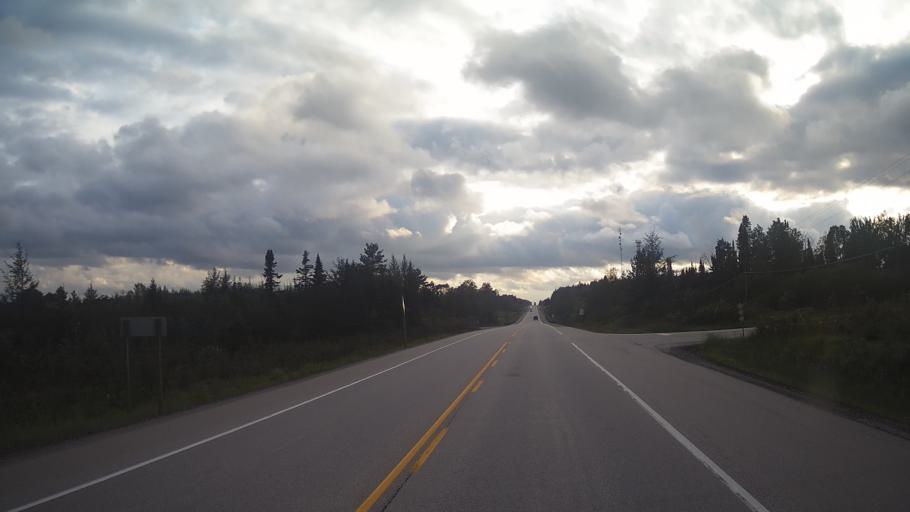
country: CA
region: Ontario
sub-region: Rainy River District
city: Atikokan
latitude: 49.0509
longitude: -90.4903
